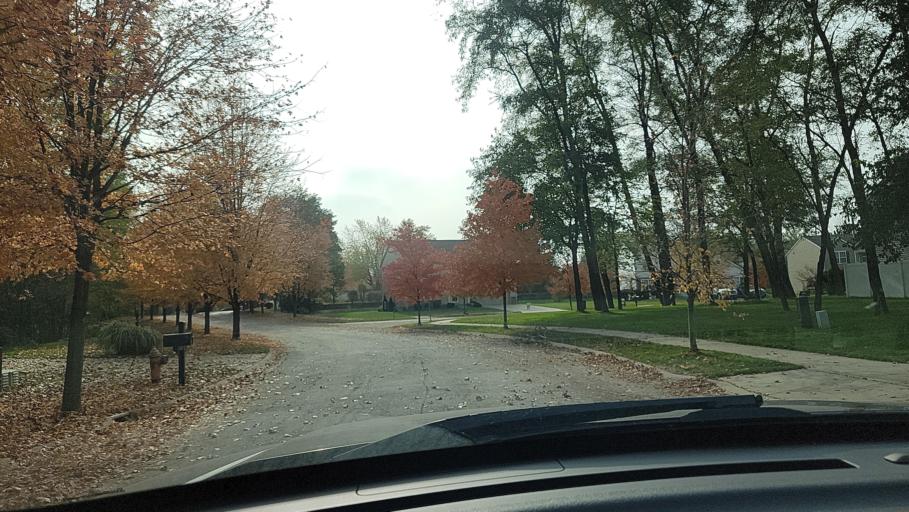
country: US
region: Indiana
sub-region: Porter County
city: Portage
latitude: 41.5953
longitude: -87.1695
